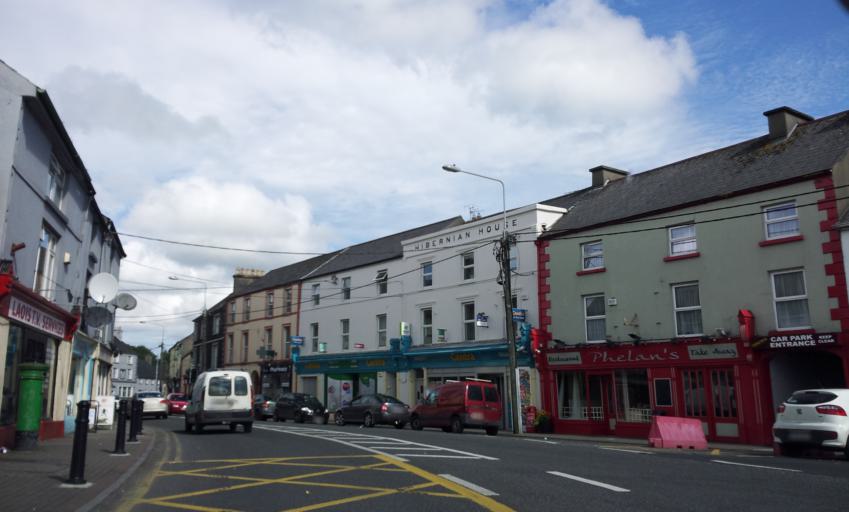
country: IE
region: Leinster
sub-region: Laois
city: Mountrath
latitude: 53.0012
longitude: -7.4745
